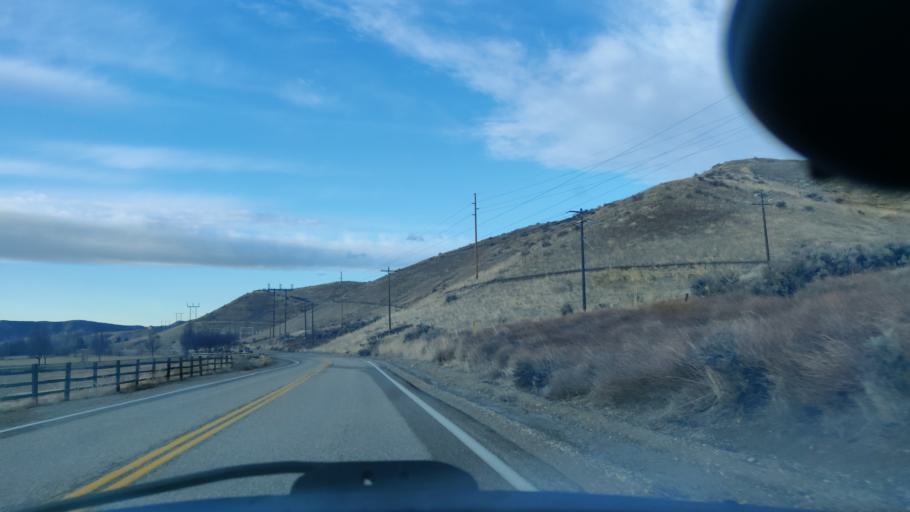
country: US
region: Idaho
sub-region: Ada County
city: Garden City
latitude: 43.7228
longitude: -116.2438
